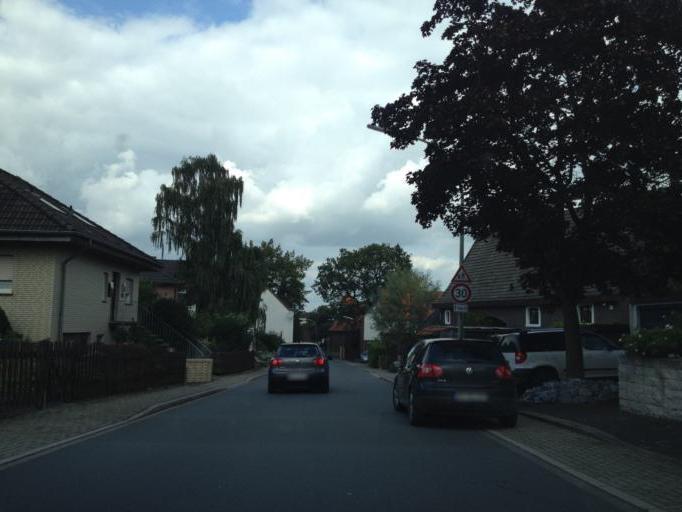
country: DE
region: North Rhine-Westphalia
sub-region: Regierungsbezirk Arnsberg
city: Soest
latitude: 51.5318
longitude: 8.0794
